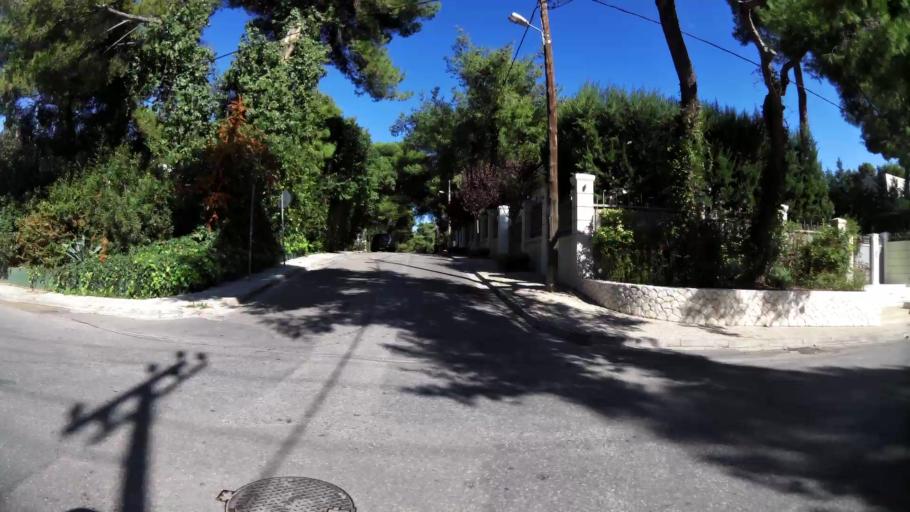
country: GR
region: Attica
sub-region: Nomarchia Athinas
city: Ekali
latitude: 38.1177
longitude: 23.8350
